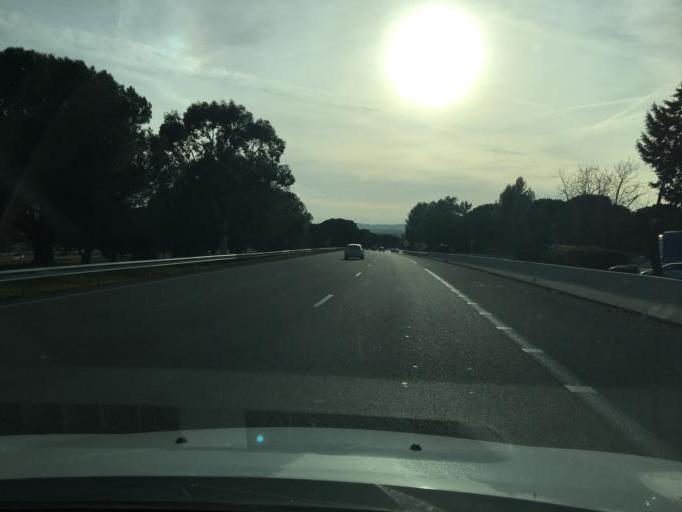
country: FR
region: Provence-Alpes-Cote d'Azur
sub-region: Departement du Var
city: Vidauban
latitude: 43.4157
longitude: 6.4531
